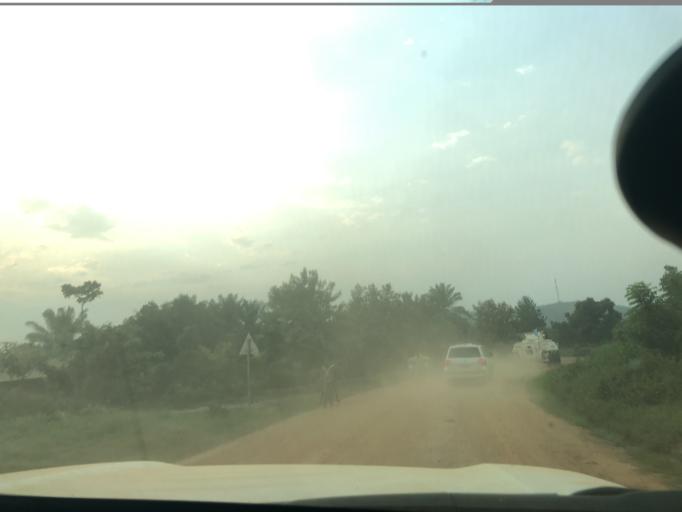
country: CD
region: Nord Kivu
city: Beni
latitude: 0.3644
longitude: 29.6205
